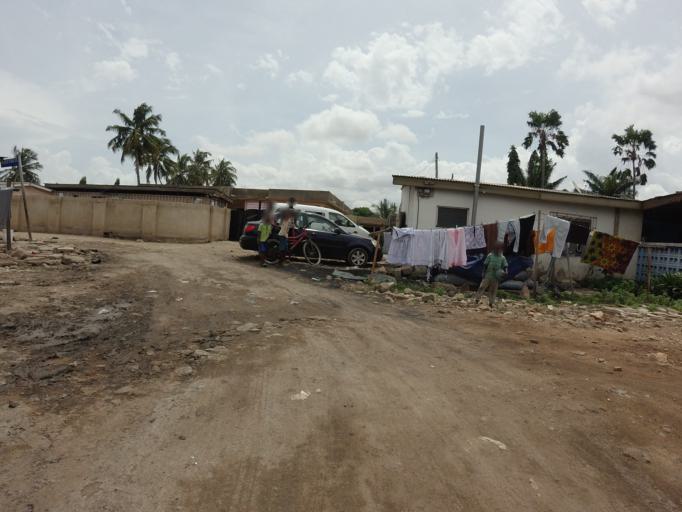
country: GH
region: Greater Accra
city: Accra
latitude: 5.6034
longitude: -0.2081
